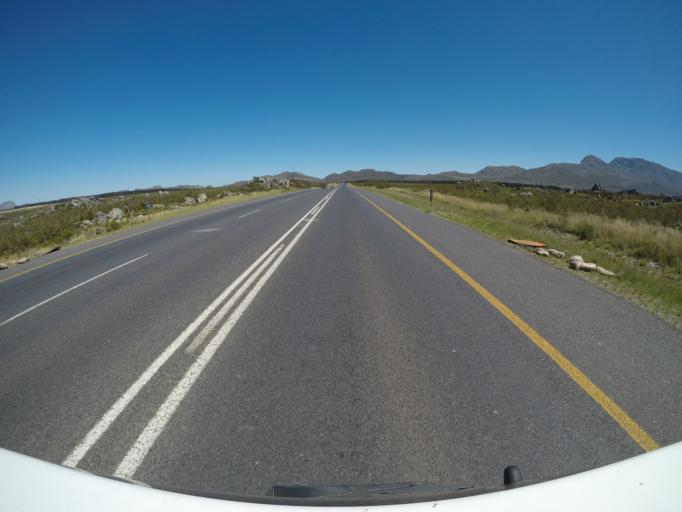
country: ZA
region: Western Cape
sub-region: Overberg District Municipality
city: Grabouw
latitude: -34.1586
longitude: 18.9751
